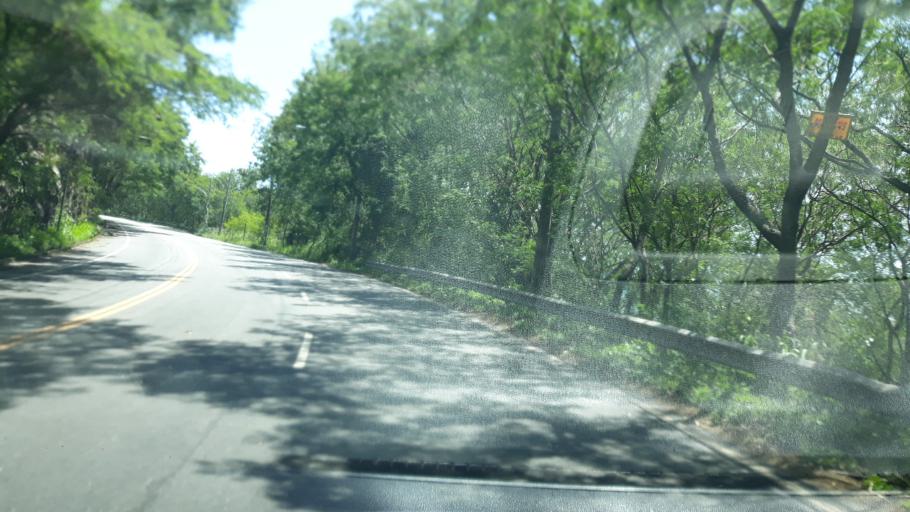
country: BR
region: Rio de Janeiro
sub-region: Nilopolis
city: Nilopolis
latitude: -23.0094
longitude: -43.5133
